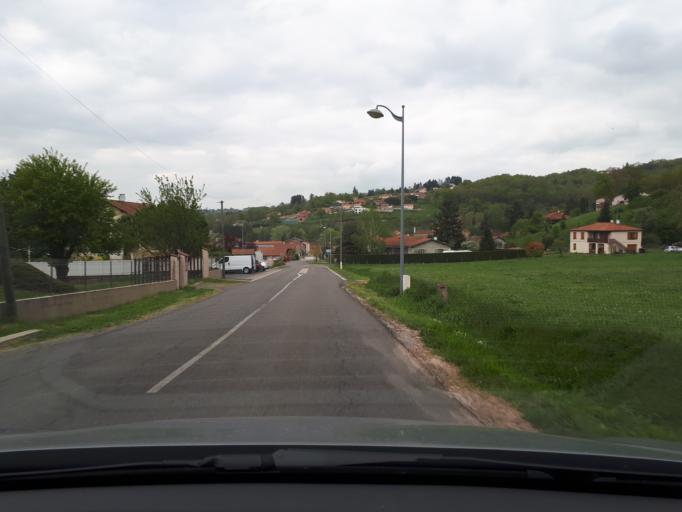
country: FR
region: Rhone-Alpes
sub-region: Departement de la Loire
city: Civens
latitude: 45.7342
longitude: 4.2884
